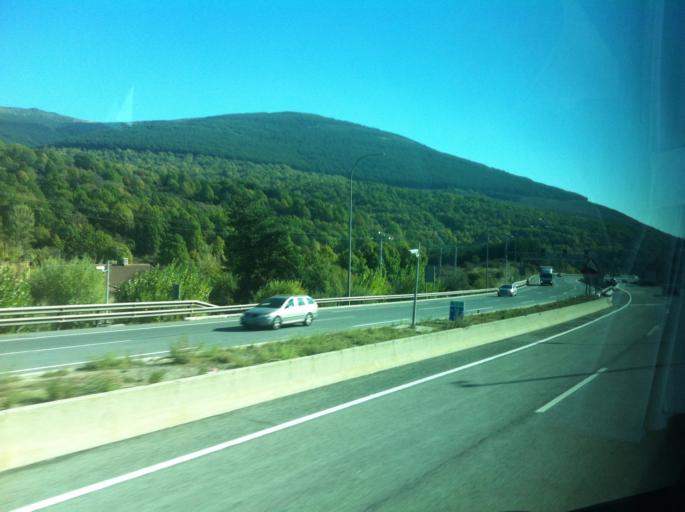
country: ES
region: Madrid
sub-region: Provincia de Madrid
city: Somosierra
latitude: 41.1307
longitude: -3.5841
